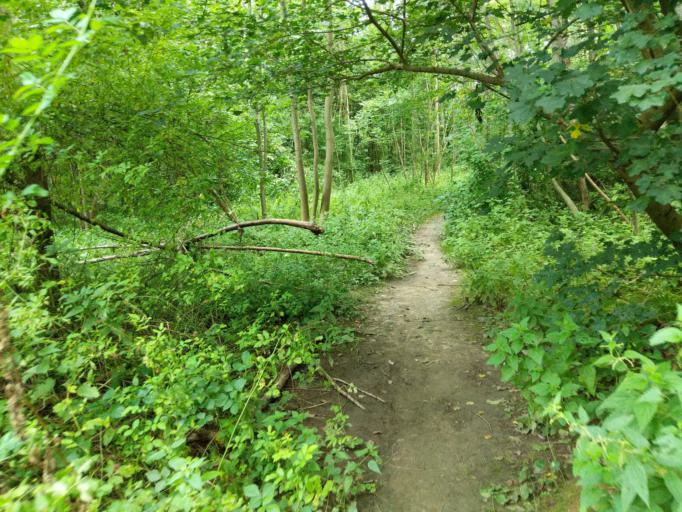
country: DE
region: Bavaria
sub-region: Upper Bavaria
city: Zorneding
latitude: 48.0916
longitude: 11.8323
